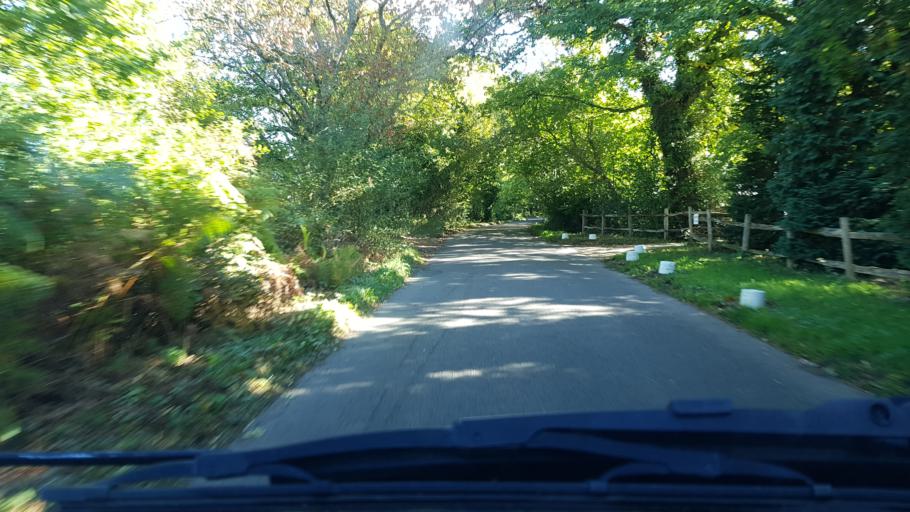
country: GB
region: England
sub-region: Surrey
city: Chiddingfold
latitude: 51.0879
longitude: -0.5880
